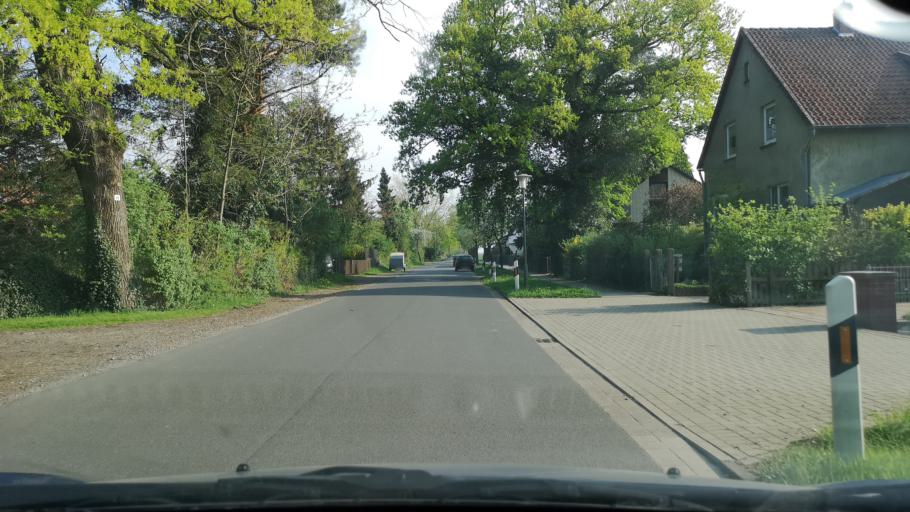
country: DE
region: Lower Saxony
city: Garbsen-Mitte
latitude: 52.4458
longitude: 9.6523
